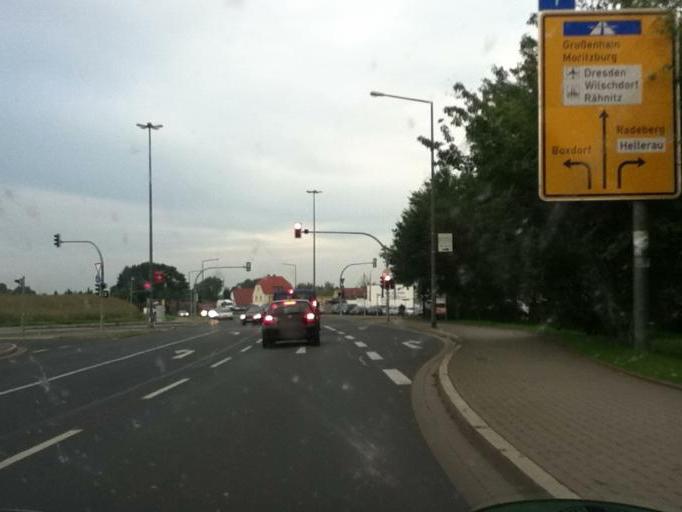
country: DE
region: Saxony
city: Albertstadt
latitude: 51.1175
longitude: 13.7304
